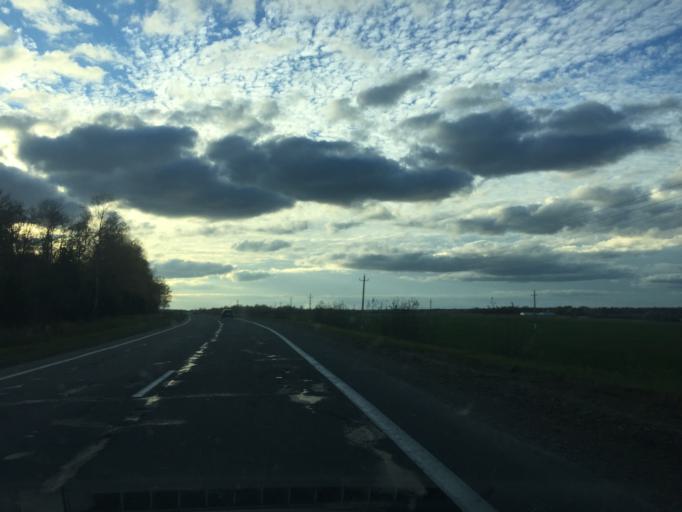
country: BY
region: Vitebsk
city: Myory
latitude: 55.8213
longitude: 27.7179
